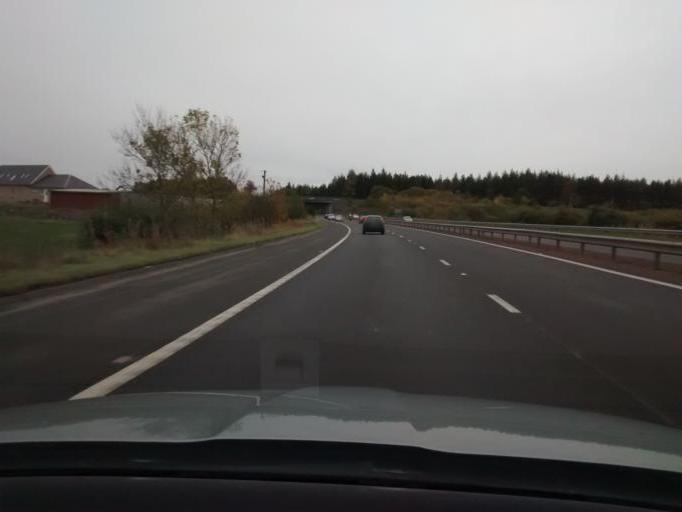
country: GB
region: Scotland
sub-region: Falkirk
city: Larbert
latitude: 56.0451
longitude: -3.8249
